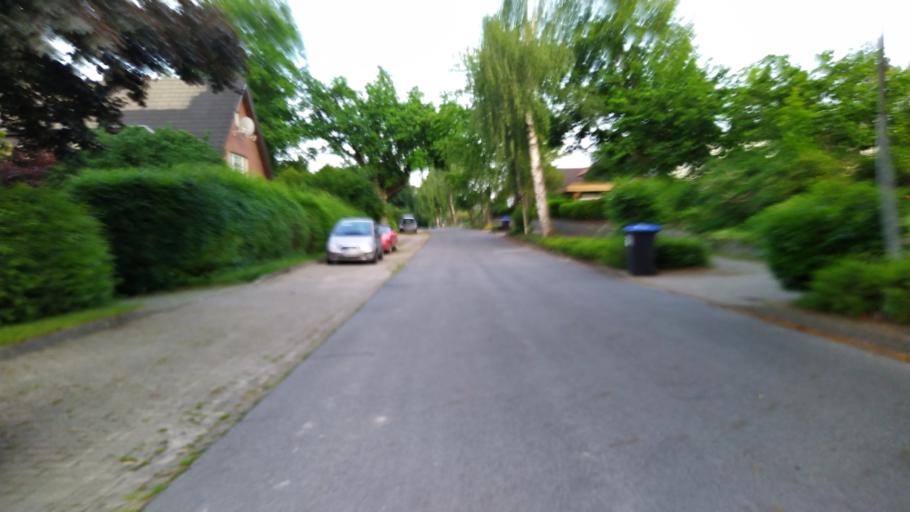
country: DE
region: Lower Saxony
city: Harsefeld
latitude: 53.4819
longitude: 9.5154
